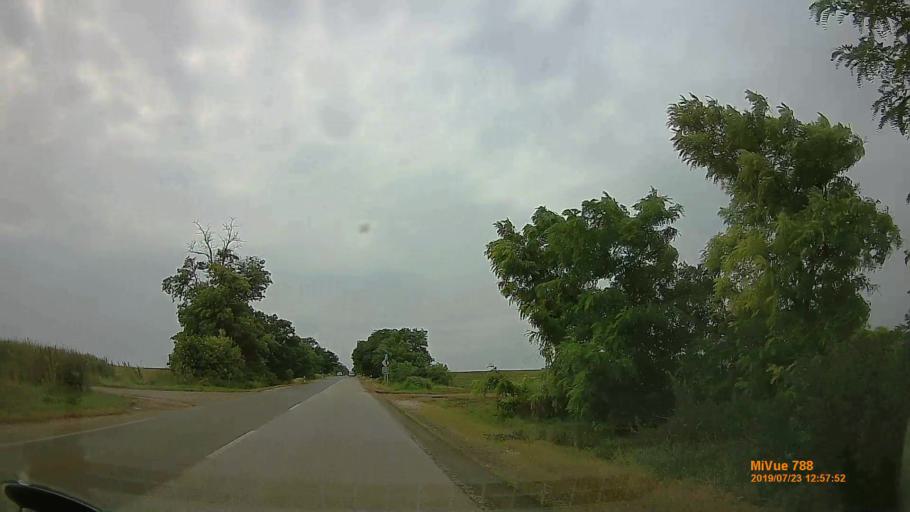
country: HU
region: Szabolcs-Szatmar-Bereg
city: Nagycserkesz
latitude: 47.9584
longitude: 21.4687
